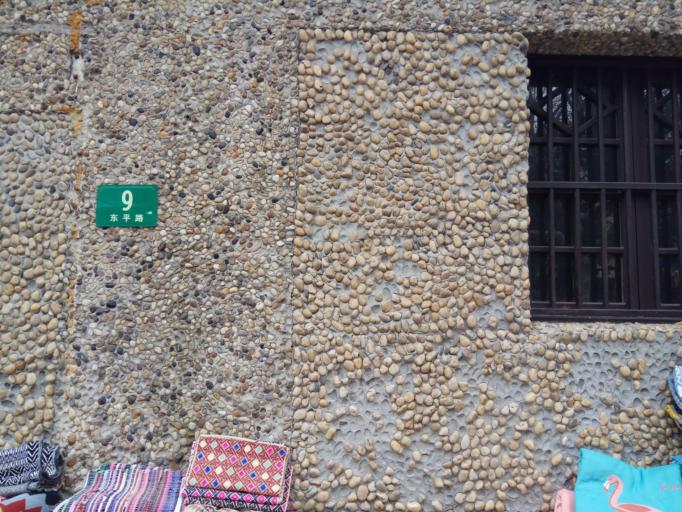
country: CN
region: Shanghai Shi
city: Xuhui
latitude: 31.2104
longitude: 121.4454
